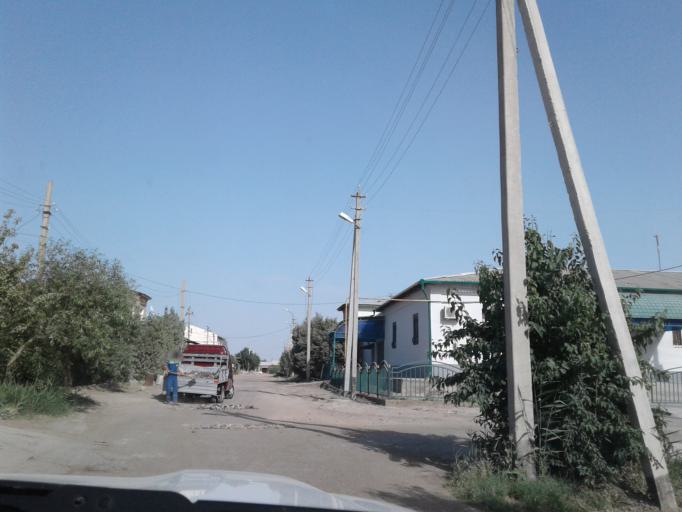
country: TM
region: Dasoguz
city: Dasoguz
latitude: 41.8489
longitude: 59.9233
